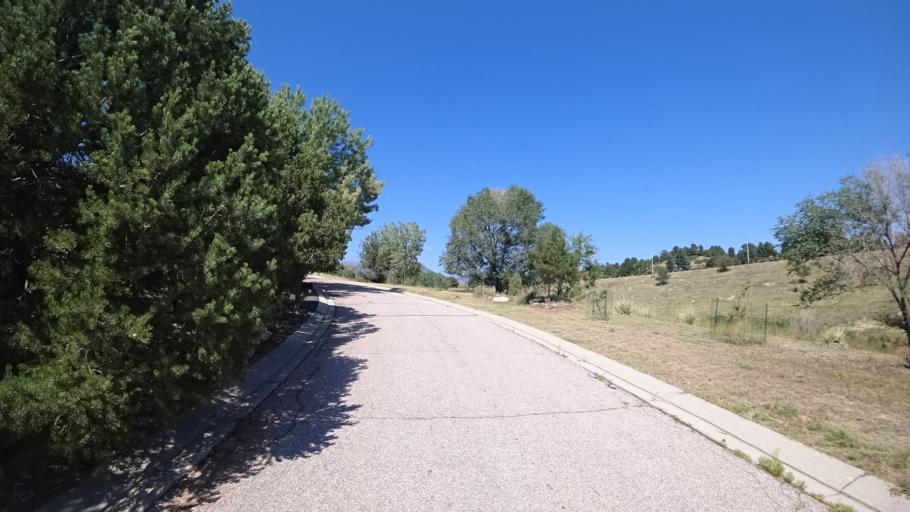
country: US
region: Colorado
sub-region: El Paso County
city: Air Force Academy
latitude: 38.9282
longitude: -104.8222
